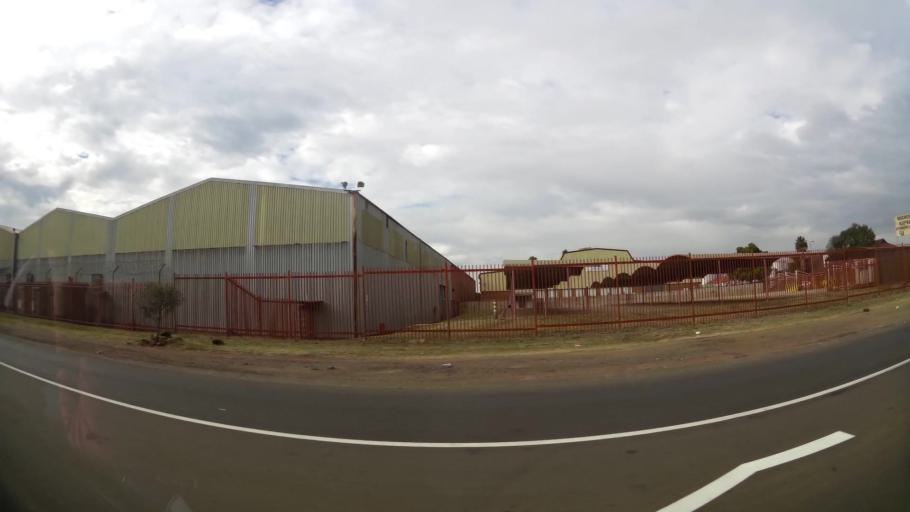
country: ZA
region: Gauteng
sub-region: City of Tshwane Metropolitan Municipality
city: Pretoria
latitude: -25.7237
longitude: 28.3112
